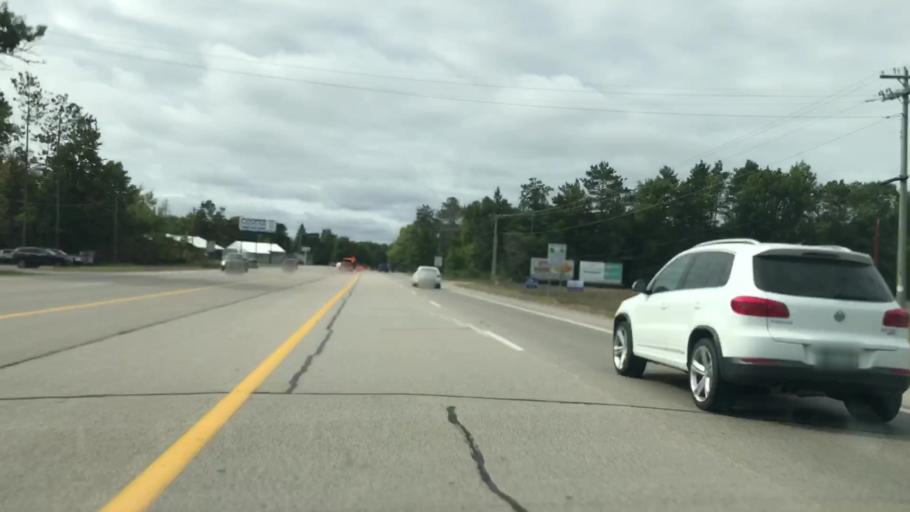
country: US
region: Michigan
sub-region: Delta County
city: Escanaba
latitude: 45.8036
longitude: -87.0645
